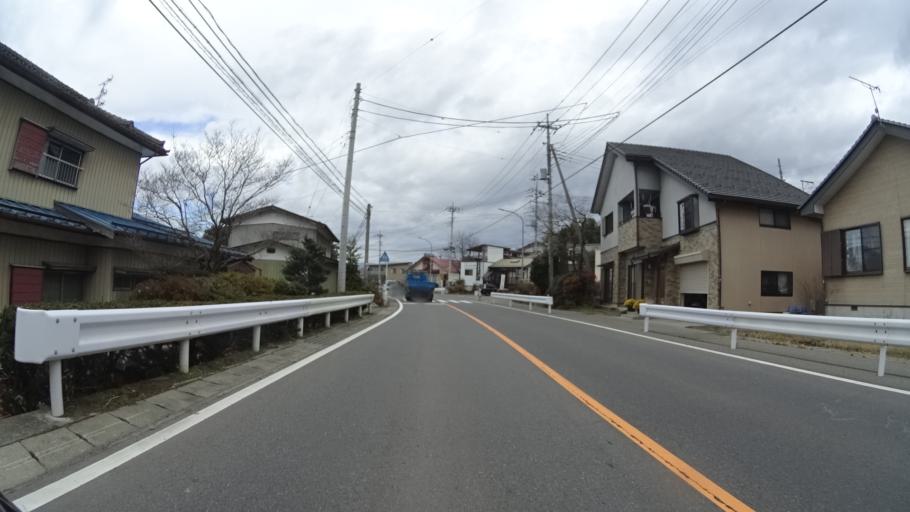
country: JP
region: Gunma
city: Numata
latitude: 36.6633
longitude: 139.1449
